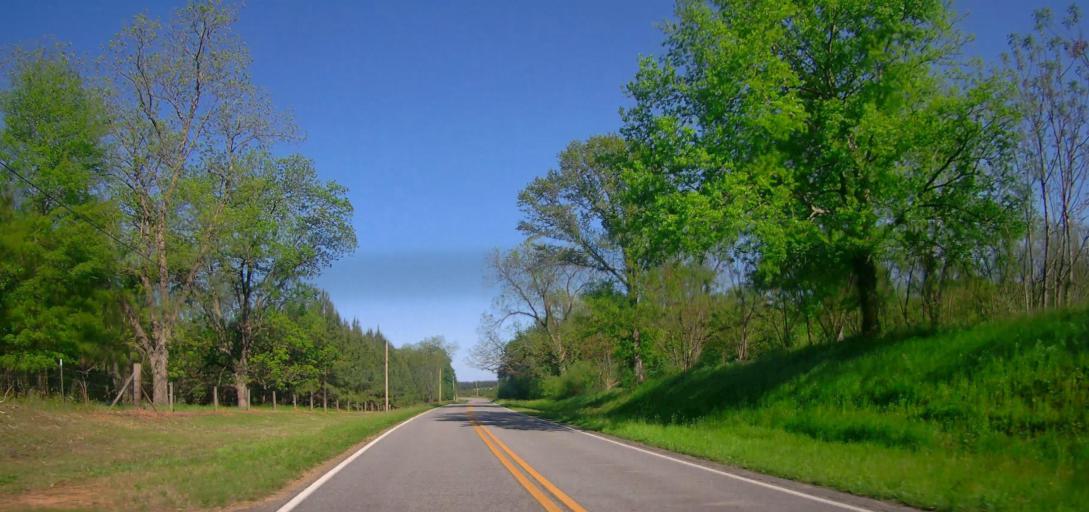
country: US
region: Georgia
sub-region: Houston County
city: Perry
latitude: 32.4513
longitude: -83.6388
